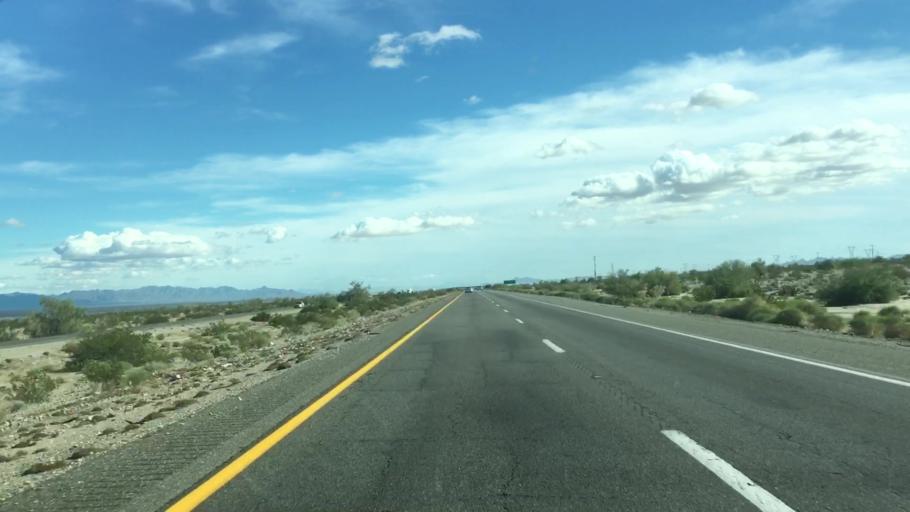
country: US
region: California
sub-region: Imperial County
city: Niland
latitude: 33.6886
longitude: -115.2648
